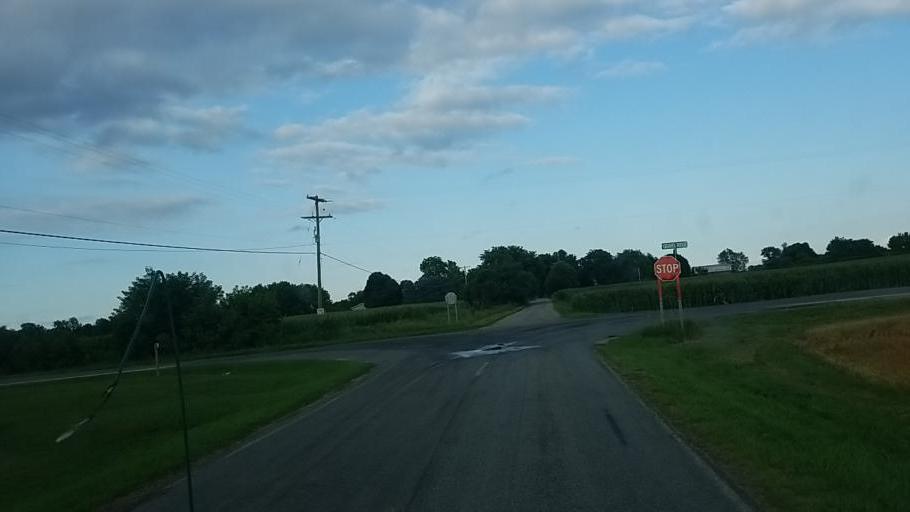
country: US
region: Michigan
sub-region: Montcalm County
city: Lakeview
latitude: 43.3377
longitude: -85.3240
